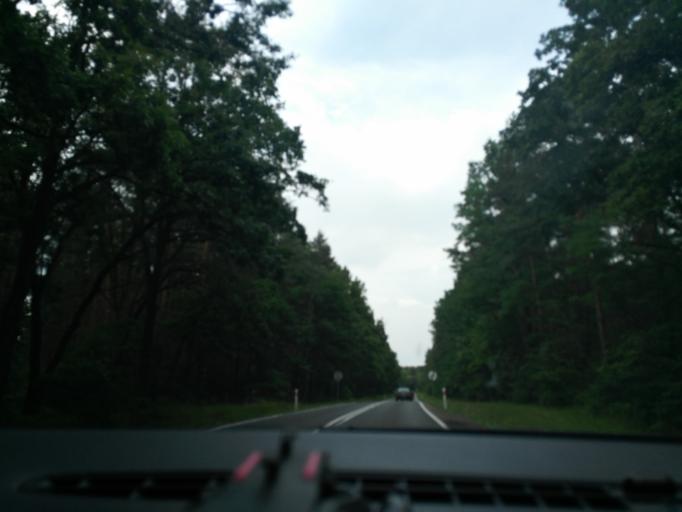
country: PL
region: Subcarpathian Voivodeship
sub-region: Powiat nizanski
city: Jezowe
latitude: 50.4040
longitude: 22.1311
